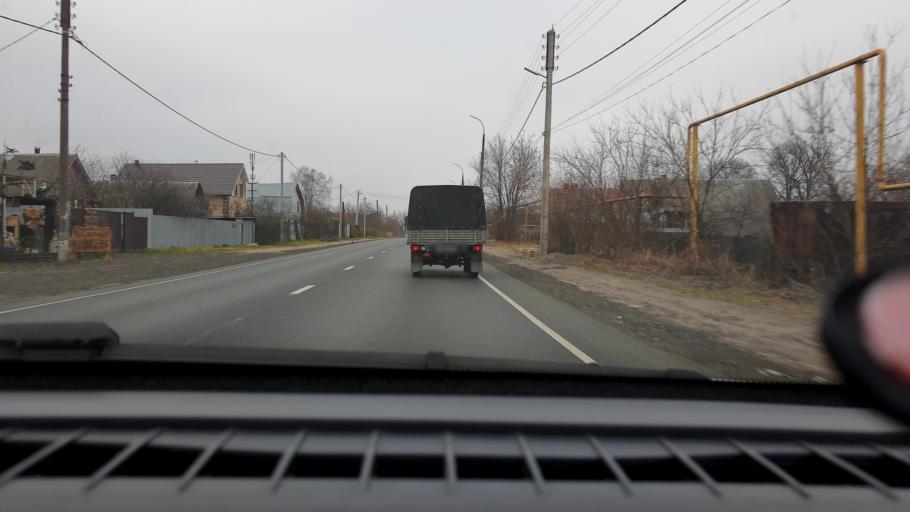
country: RU
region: Nizjnij Novgorod
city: Gidrotorf
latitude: 56.5355
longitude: 43.5386
